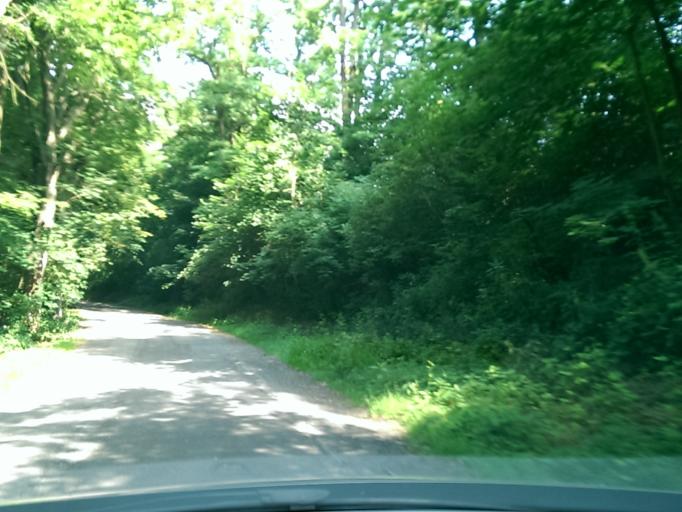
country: CZ
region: Central Bohemia
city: Bakov nad Jizerou
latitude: 50.4767
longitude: 14.9257
